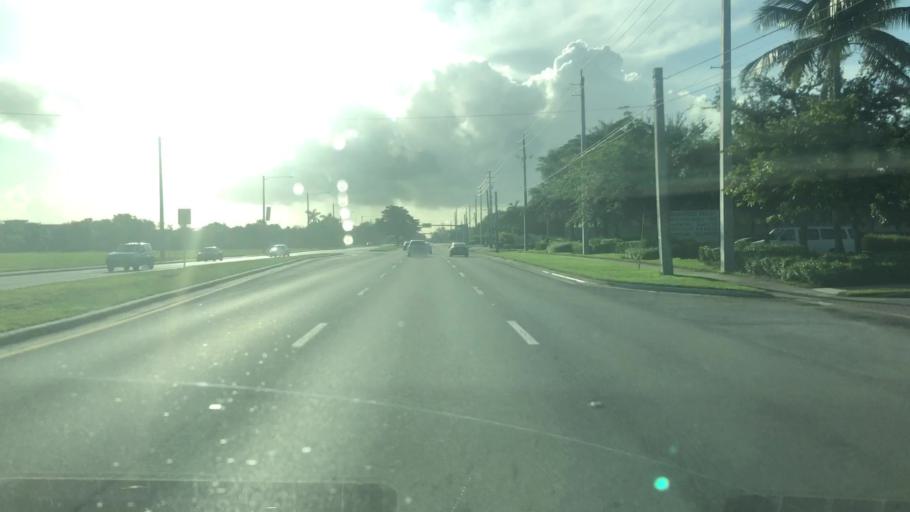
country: US
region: Florida
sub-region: Broward County
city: Tamarac
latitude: 26.1936
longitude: -80.2732
